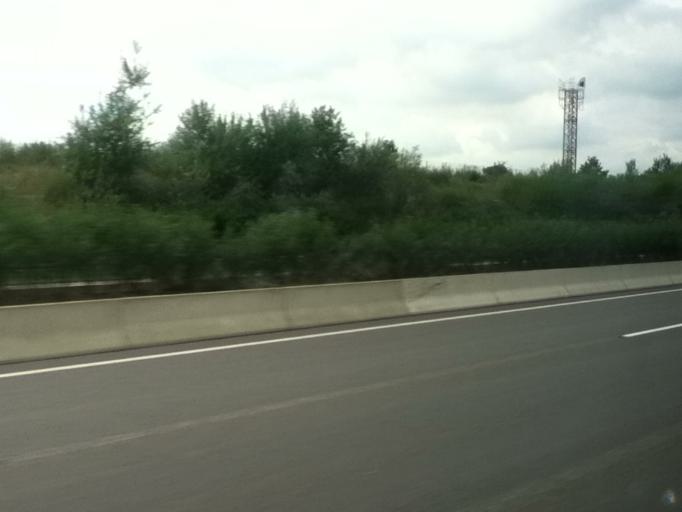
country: DE
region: Thuringia
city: Zollnitz
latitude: 50.8789
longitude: 11.6259
